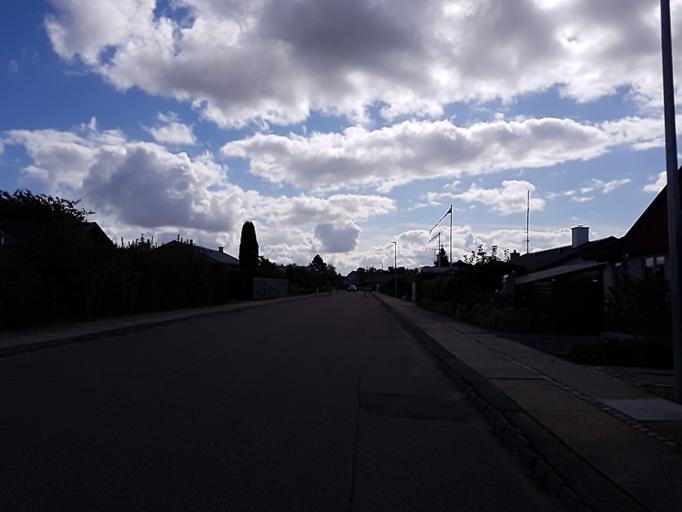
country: DK
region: Capital Region
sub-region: Egedal Kommune
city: Olstykke
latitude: 55.7906
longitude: 12.1440
